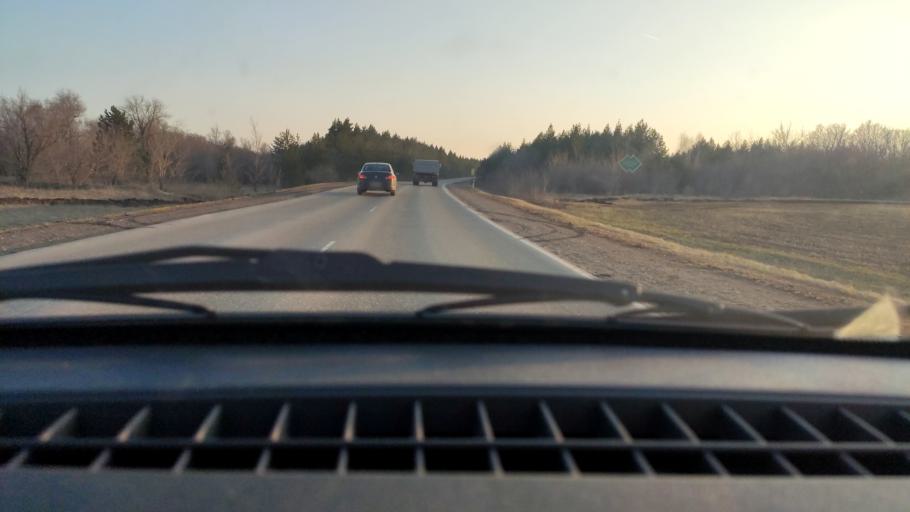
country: RU
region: Bashkortostan
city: Davlekanovo
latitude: 54.2481
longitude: 55.0783
